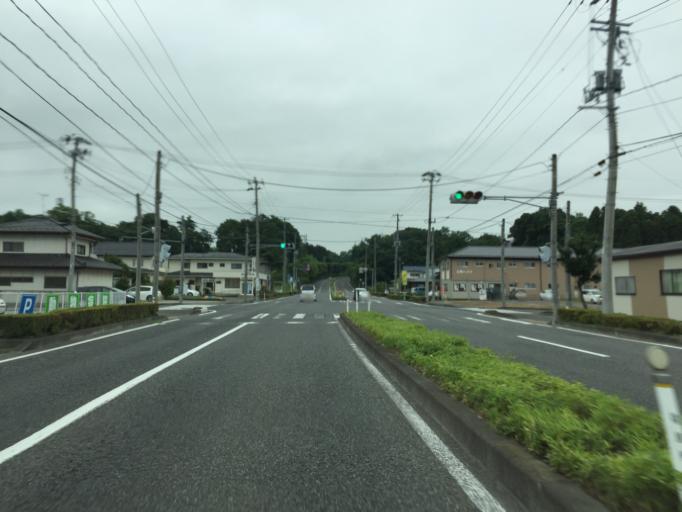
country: JP
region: Fukushima
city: Sukagawa
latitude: 37.2841
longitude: 140.3585
